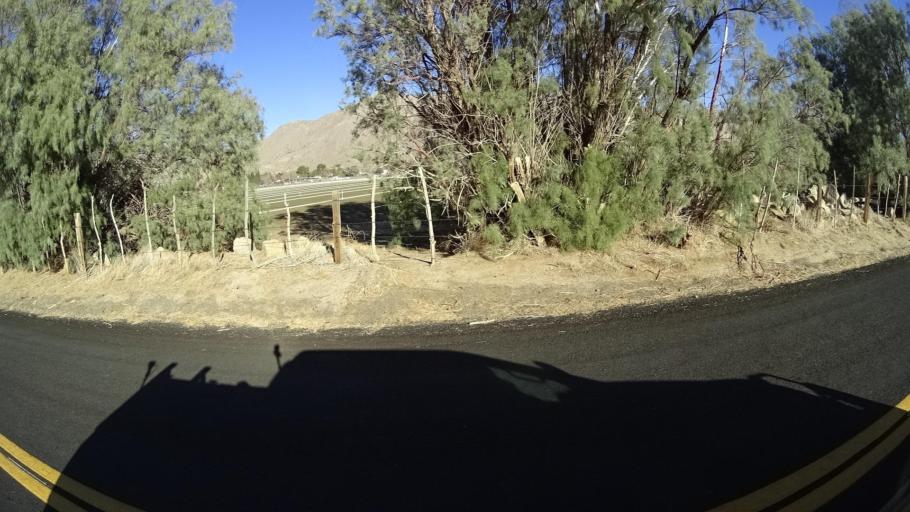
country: US
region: California
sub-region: Kern County
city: Weldon
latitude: 35.6473
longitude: -118.2719
